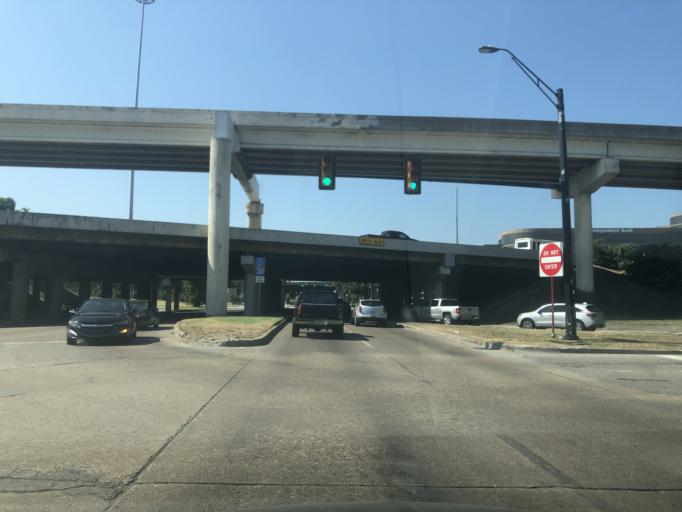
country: US
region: Texas
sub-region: Tarrant County
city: Fort Worth
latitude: 32.7343
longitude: -97.3615
